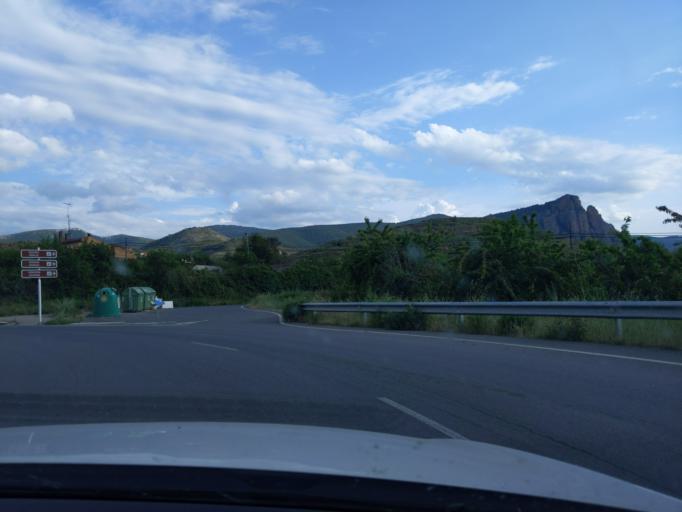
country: ES
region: La Rioja
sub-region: Provincia de La Rioja
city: Nalda
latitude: 42.3368
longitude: -2.4932
